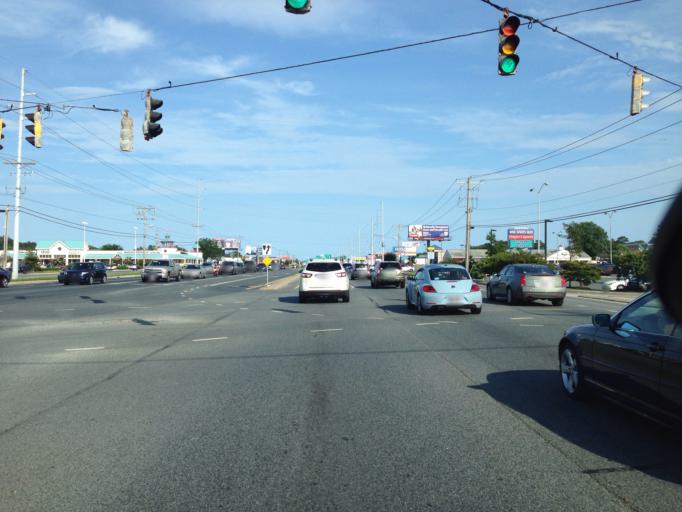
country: US
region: Delaware
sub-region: Sussex County
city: Rehoboth Beach
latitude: 38.7180
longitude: -75.1135
